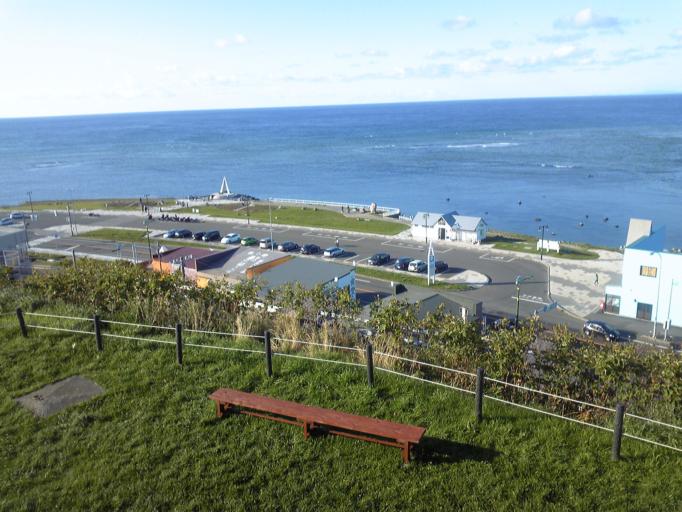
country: JP
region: Hokkaido
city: Makubetsu
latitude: 45.5208
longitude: 141.9375
